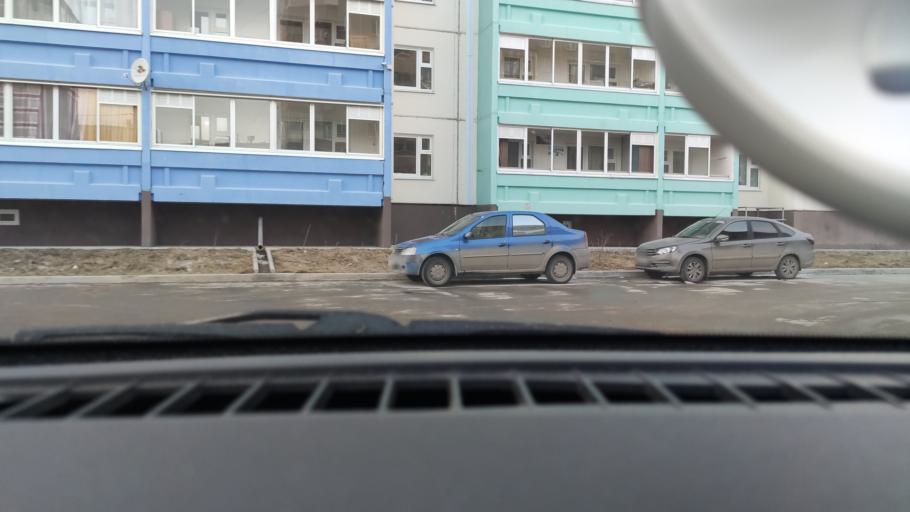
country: RU
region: Perm
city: Perm
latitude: 58.0866
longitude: 56.4082
